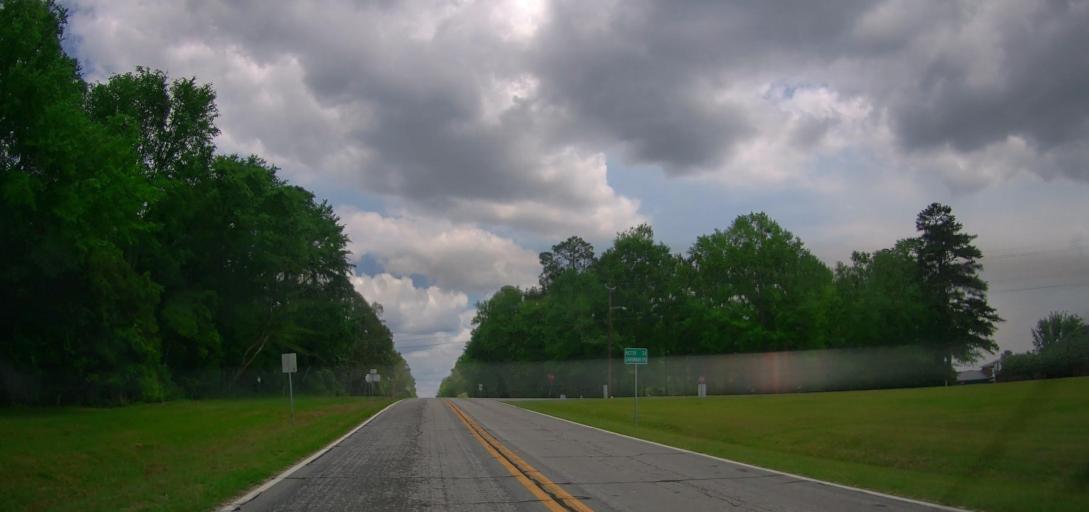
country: US
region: Georgia
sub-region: Treutlen County
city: Soperton
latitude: 32.3830
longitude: -82.5862
